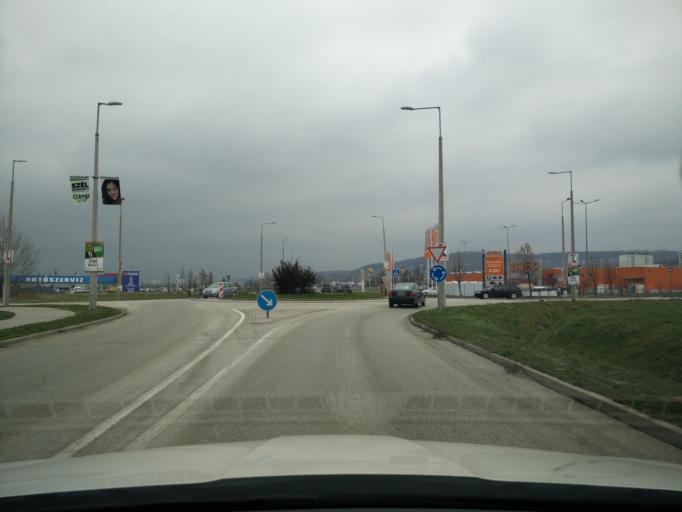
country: HU
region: Tolna
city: Szekszard
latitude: 46.3349
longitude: 18.7063
